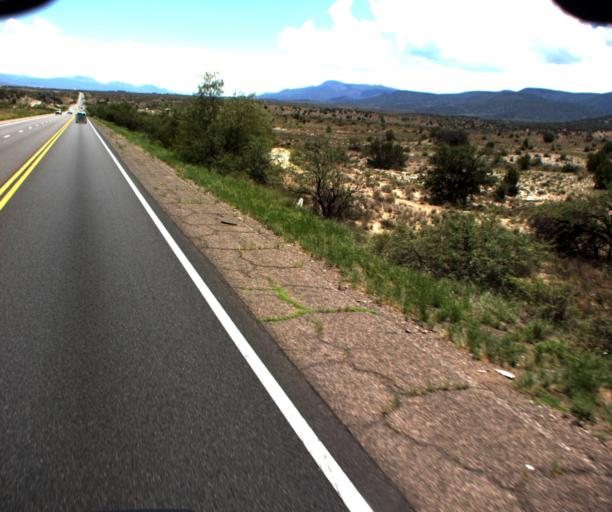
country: US
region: Arizona
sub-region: Yavapai County
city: Cornville
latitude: 34.6438
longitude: -111.9500
